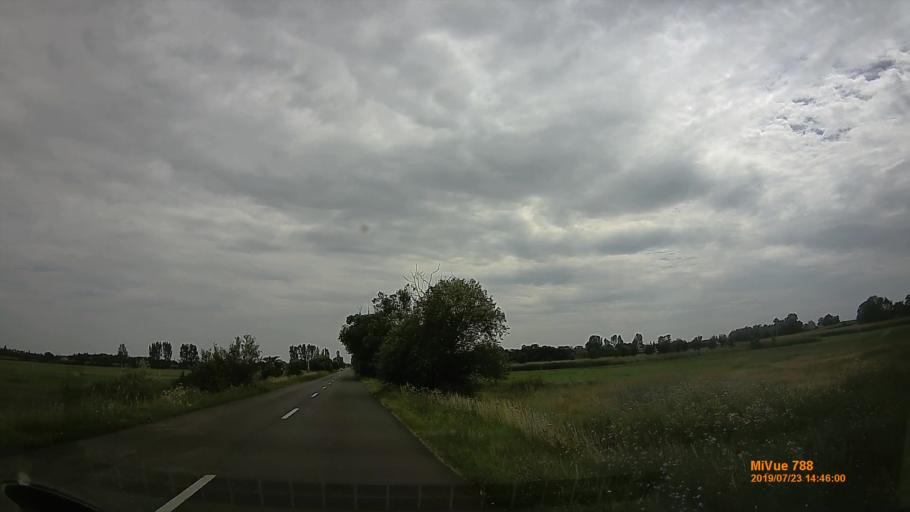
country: HU
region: Szabolcs-Szatmar-Bereg
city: Nyiregyhaza
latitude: 47.9234
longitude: 21.6772
